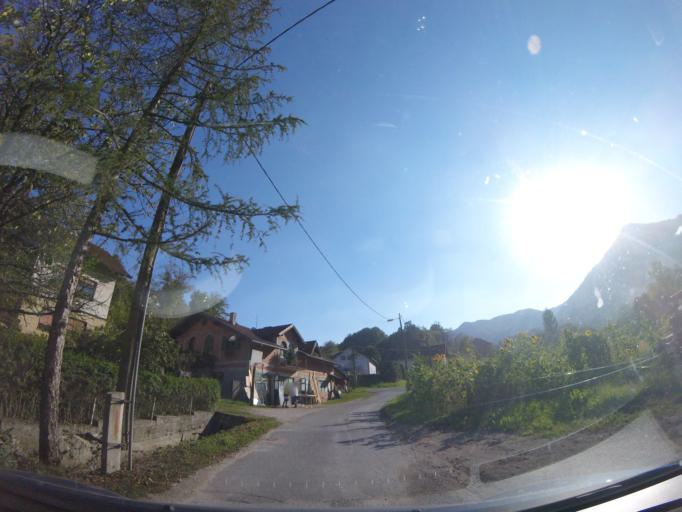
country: HR
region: Zagrebacka
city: Rude
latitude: 45.7627
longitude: 15.6668
